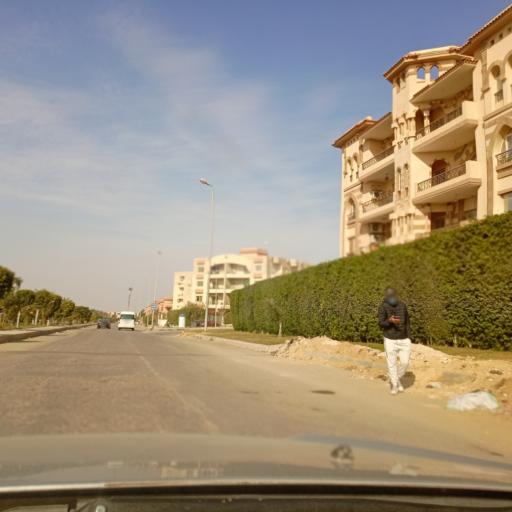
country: EG
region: Muhafazat al Qalyubiyah
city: Al Khankah
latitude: 30.0486
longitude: 31.4853
